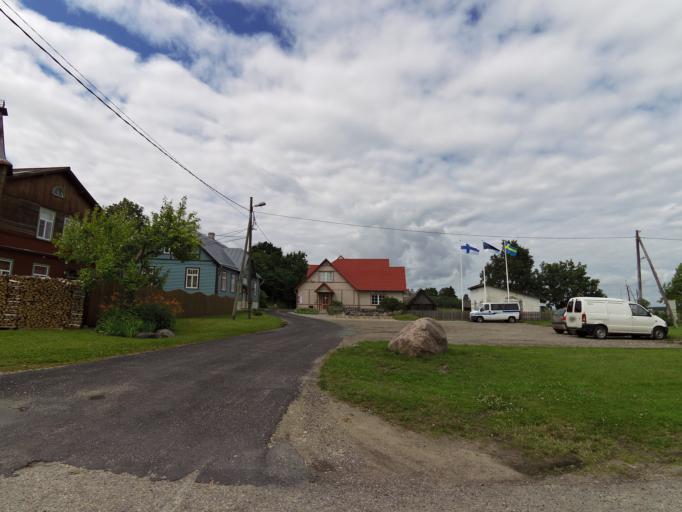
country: EE
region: Laeaene
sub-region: Haapsalu linn
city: Haapsalu
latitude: 58.9555
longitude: 23.5287
